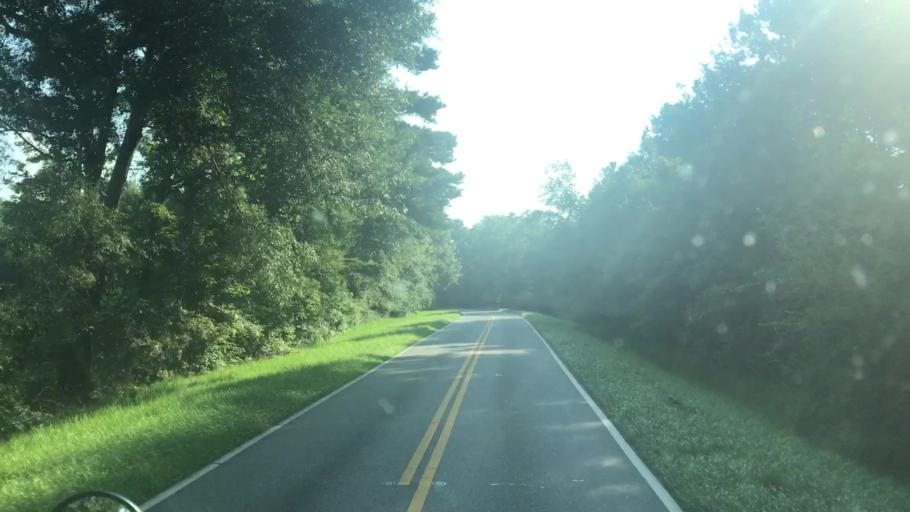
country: US
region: Florida
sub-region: Gadsden County
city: Quincy
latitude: 30.6723
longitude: -84.5438
